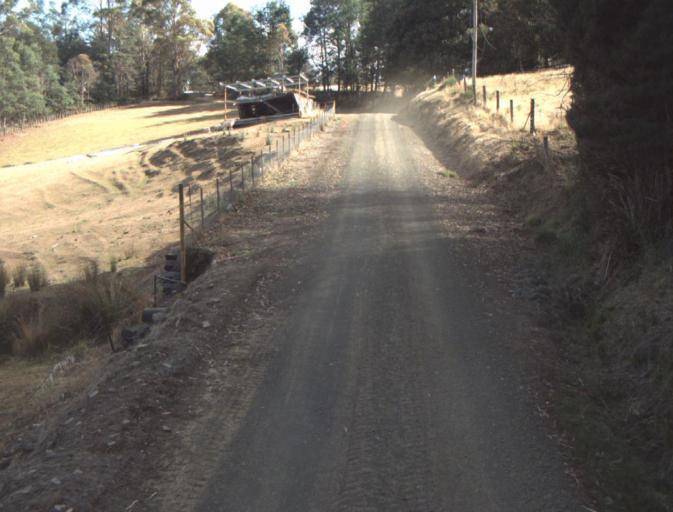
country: AU
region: Tasmania
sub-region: Launceston
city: Mayfield
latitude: -41.2958
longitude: 147.2148
